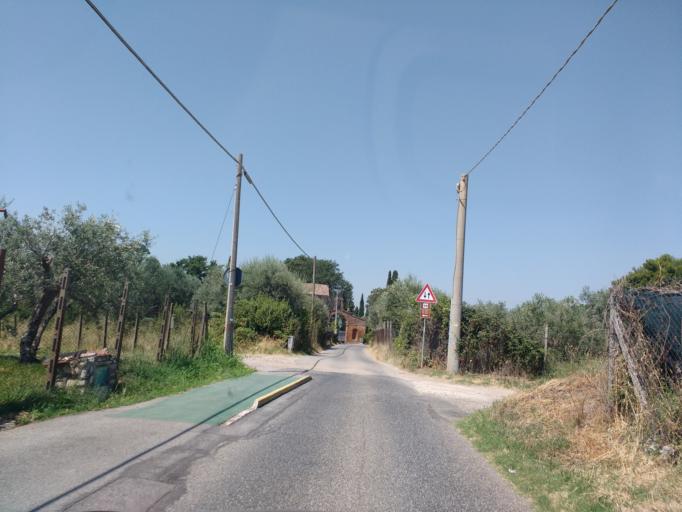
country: IT
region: Latium
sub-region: Citta metropolitana di Roma Capitale
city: Villa Adriana
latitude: 41.9478
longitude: 12.7820
